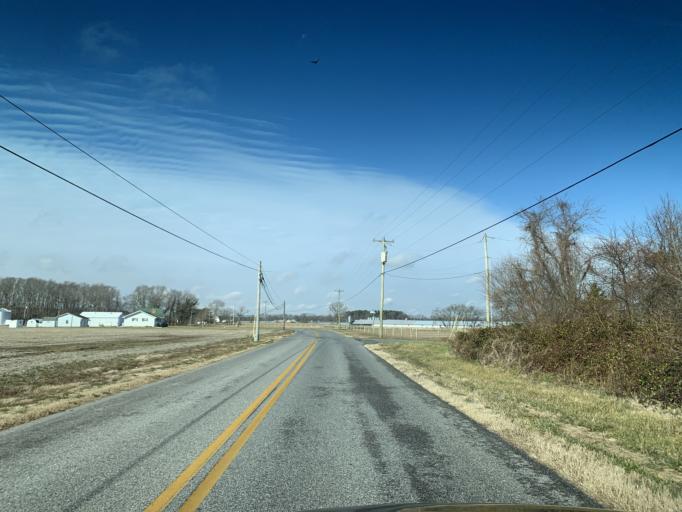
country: US
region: Maryland
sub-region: Worcester County
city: Ocean Pines
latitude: 38.4307
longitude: -75.1768
